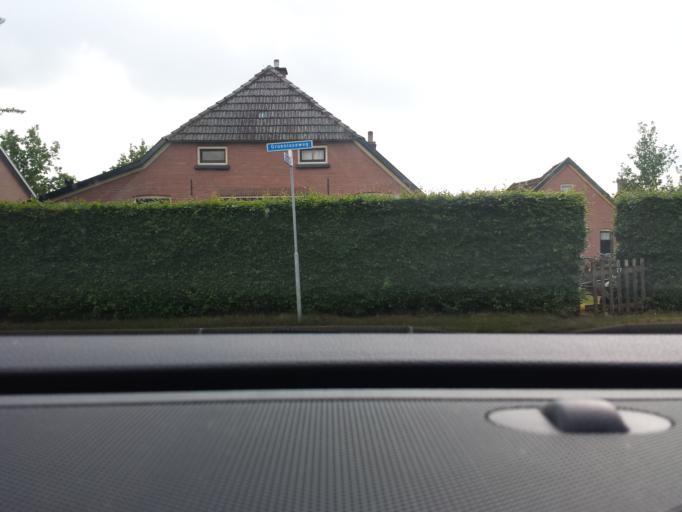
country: NL
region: Gelderland
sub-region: Gemeente Lochem
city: Barchem
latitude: 52.0793
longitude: 6.4624
